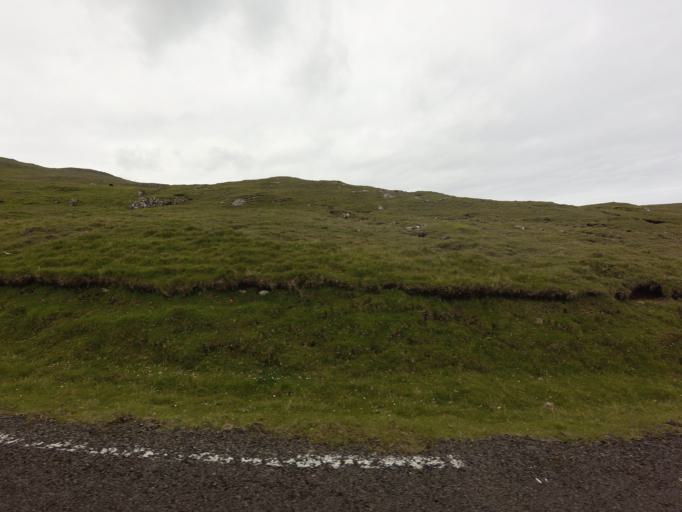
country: FO
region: Suduroy
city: Vagur
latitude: 61.4410
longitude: -6.7419
